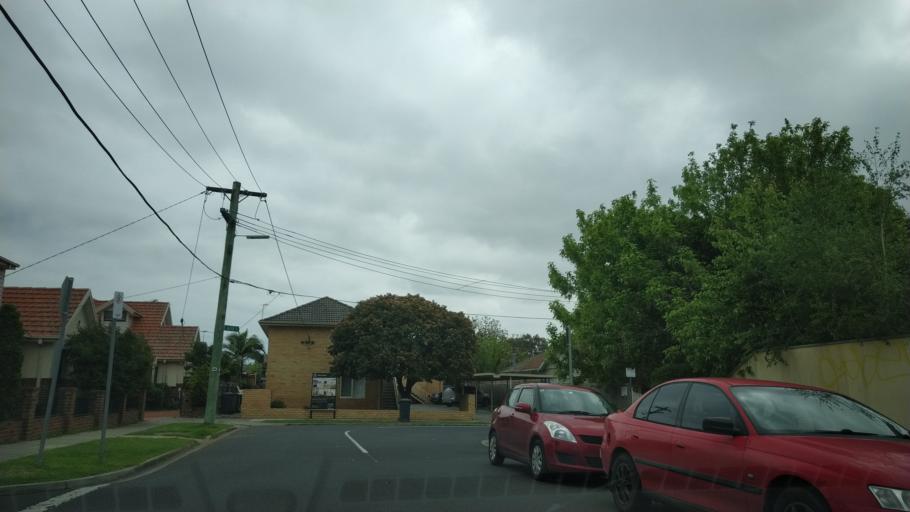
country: AU
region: Victoria
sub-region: Glen Eira
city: Murrumbeena
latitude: -37.8957
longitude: 145.0709
